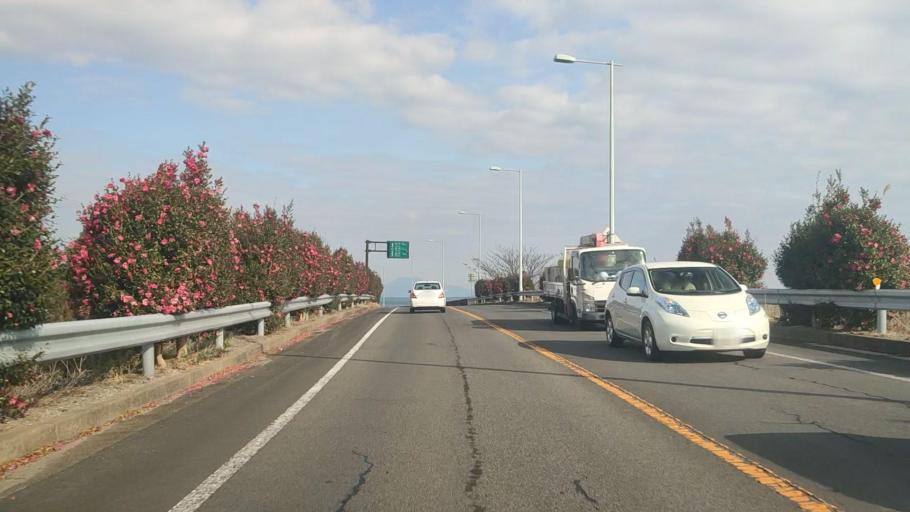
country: JP
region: Nagasaki
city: Shimabara
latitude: 32.7211
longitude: 130.3568
